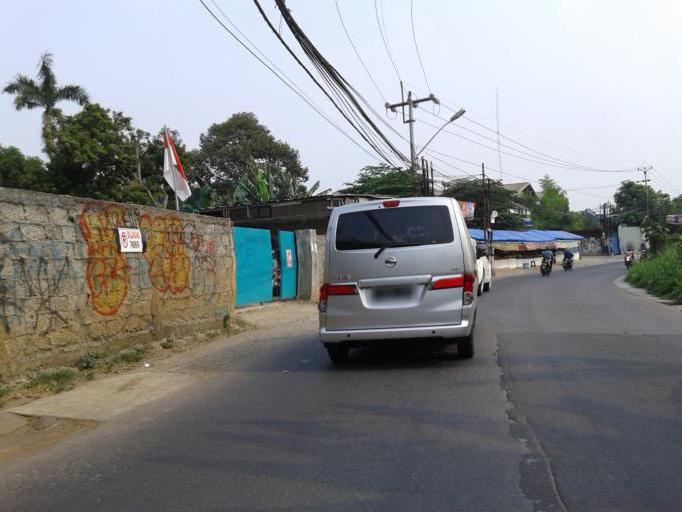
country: ID
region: West Java
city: Sawangan
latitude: -6.3618
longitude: 106.7761
